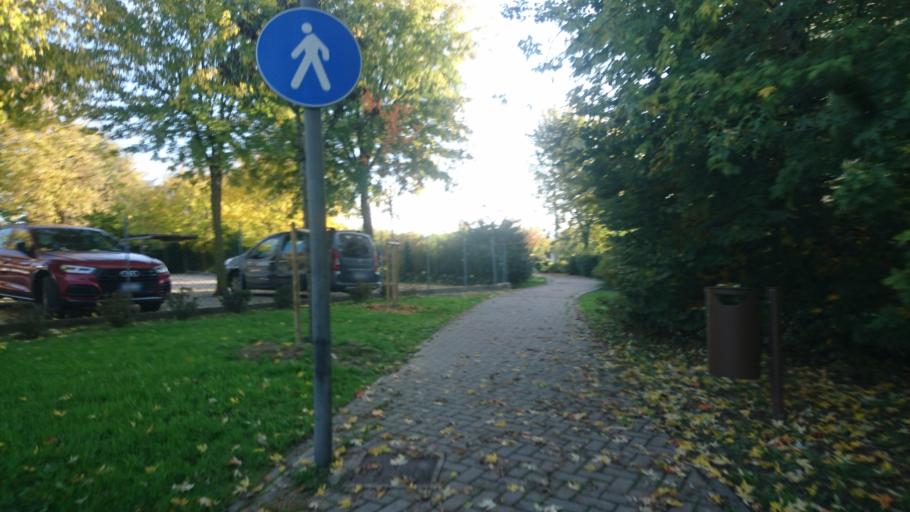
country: IT
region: Veneto
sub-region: Provincia di Padova
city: Abano Terme
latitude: 45.3473
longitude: 11.7805
